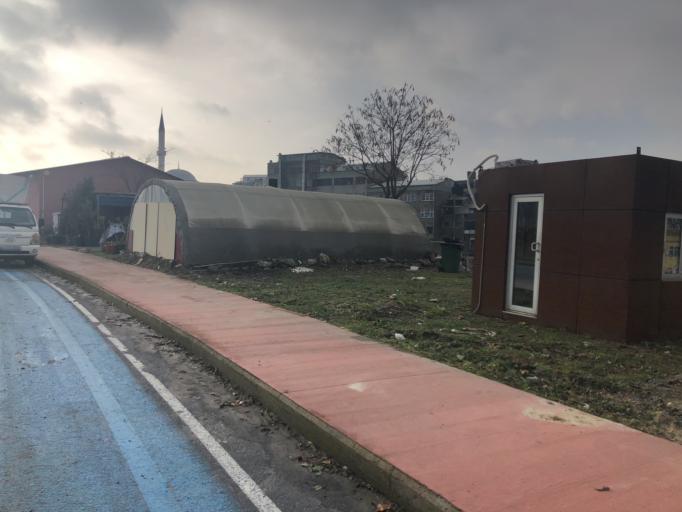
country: TR
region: Istanbul
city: merter keresteciler
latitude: 41.0225
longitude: 28.8861
